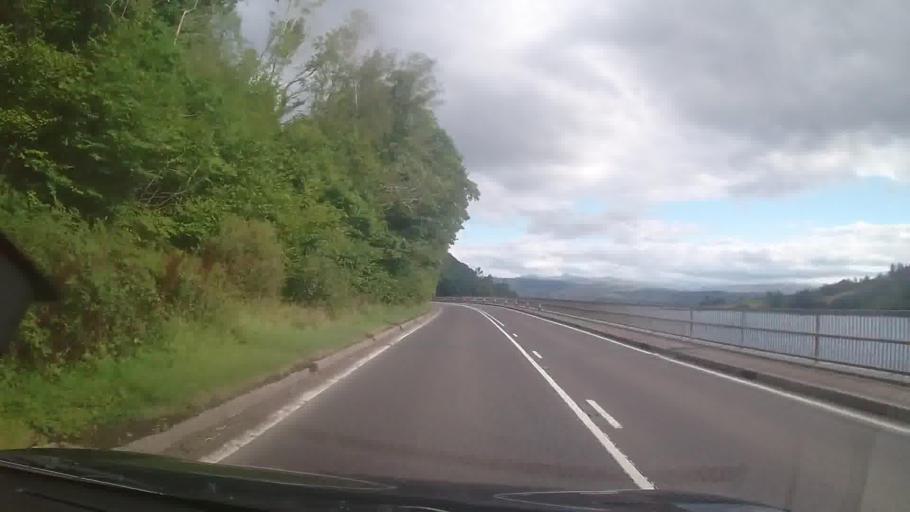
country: GB
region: Scotland
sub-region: Argyll and Bute
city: Oban
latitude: 56.3957
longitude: -5.1236
